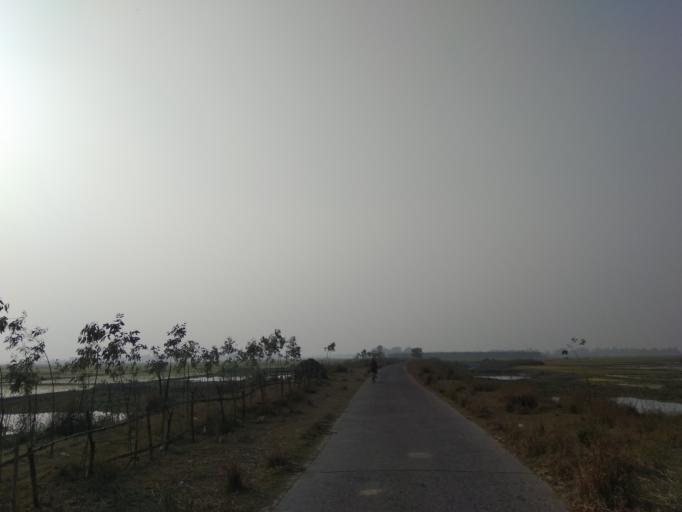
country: BD
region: Rajshahi
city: Ishurdi
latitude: 24.4954
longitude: 89.1904
